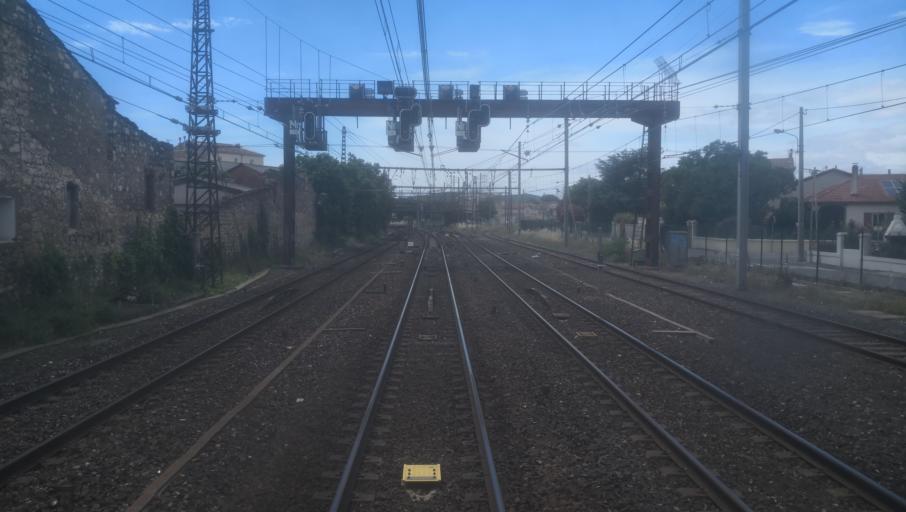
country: FR
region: Languedoc-Roussillon
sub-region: Departement de l'Aude
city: Narbonne
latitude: 43.1829
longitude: 2.9946
